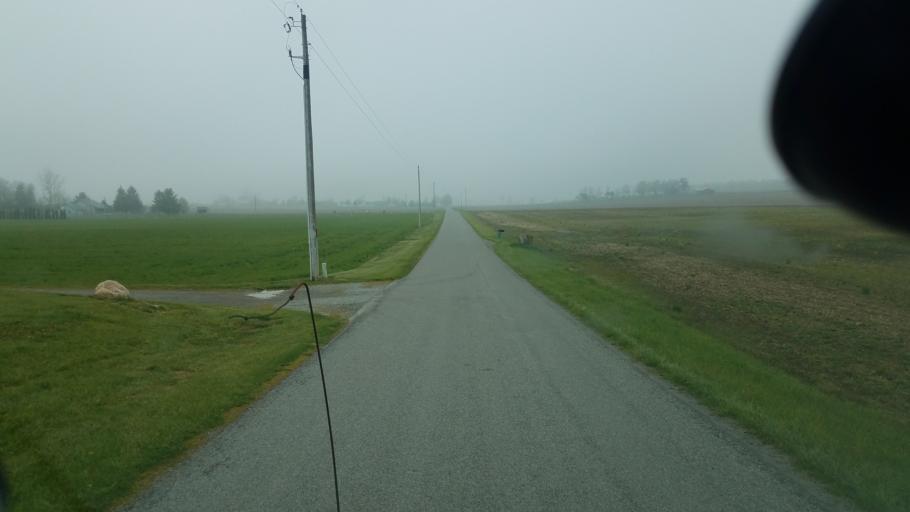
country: US
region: Ohio
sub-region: Logan County
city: Bellefontaine
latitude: 40.3993
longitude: -83.8272
